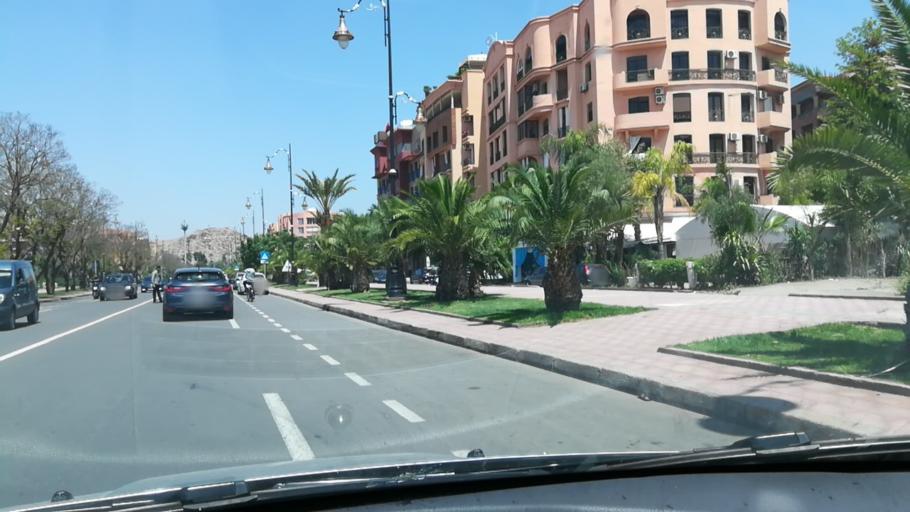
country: MA
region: Marrakech-Tensift-Al Haouz
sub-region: Marrakech
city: Marrakesh
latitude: 31.6358
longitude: -8.0198
